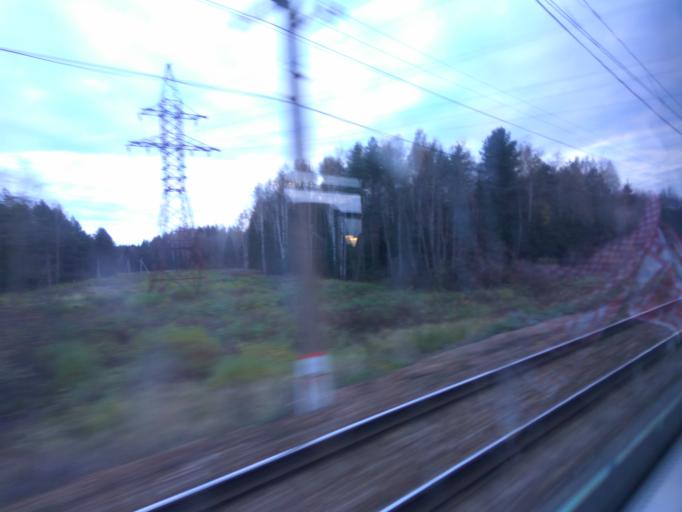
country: RU
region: Moskovskaya
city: Kievskij
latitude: 55.4761
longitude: 36.9110
